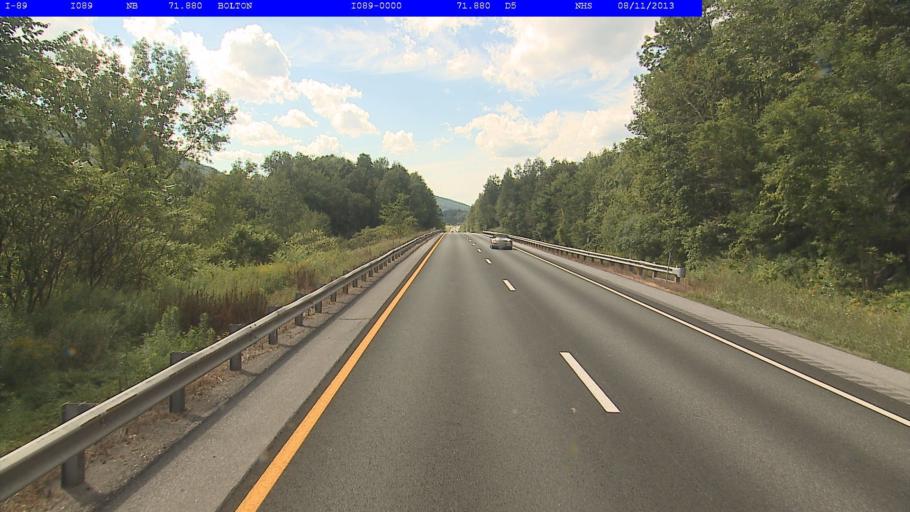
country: US
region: Vermont
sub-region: Washington County
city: Waterbury
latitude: 44.3790
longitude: -72.9037
